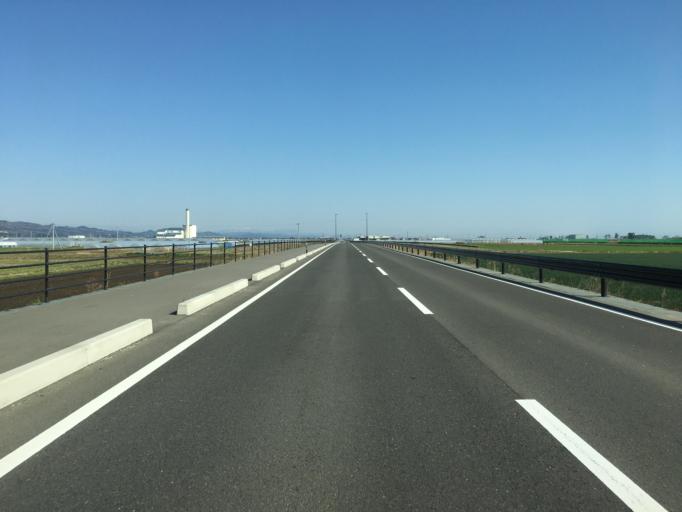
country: JP
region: Miyagi
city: Watari
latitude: 37.9484
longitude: 140.9066
